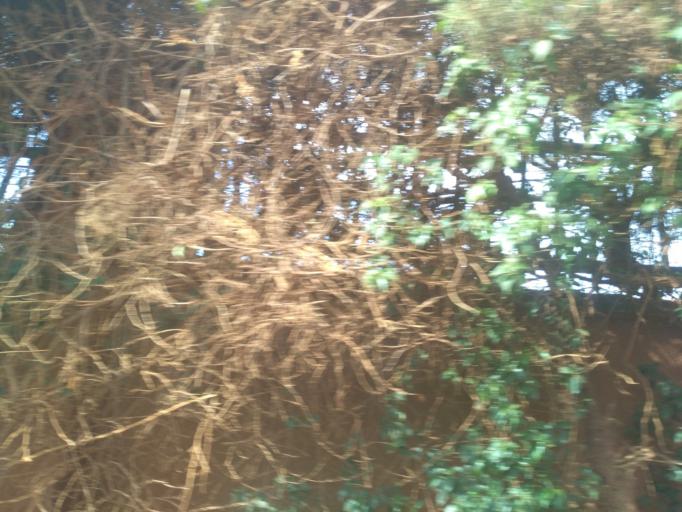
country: UG
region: Central Region
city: Kampala Central Division
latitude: 0.3593
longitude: 32.5780
